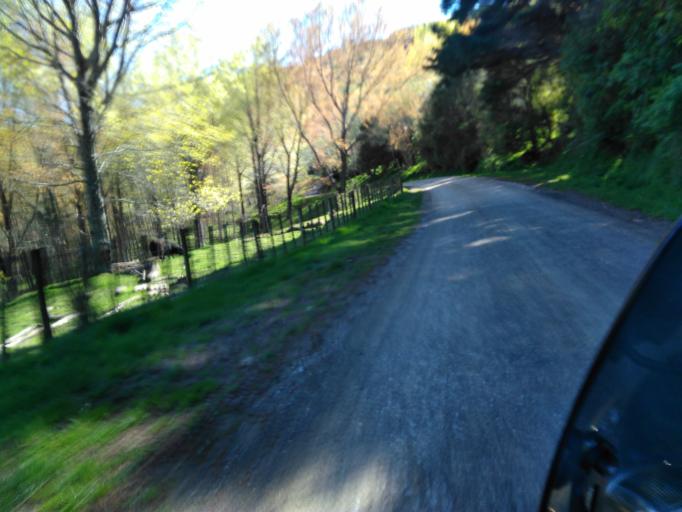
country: NZ
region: Gisborne
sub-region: Gisborne District
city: Gisborne
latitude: -38.3897
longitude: 177.6385
